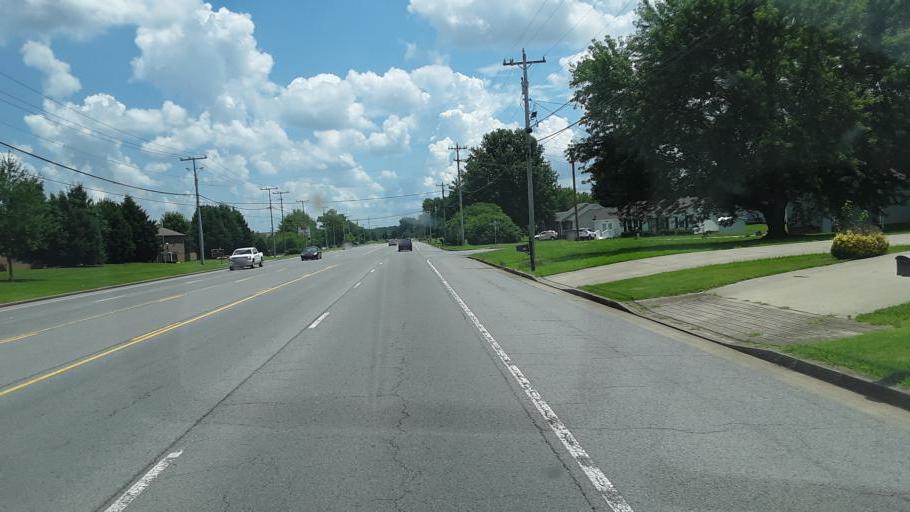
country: US
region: Kentucky
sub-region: Christian County
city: Oak Grove
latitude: 36.6309
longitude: -87.3991
